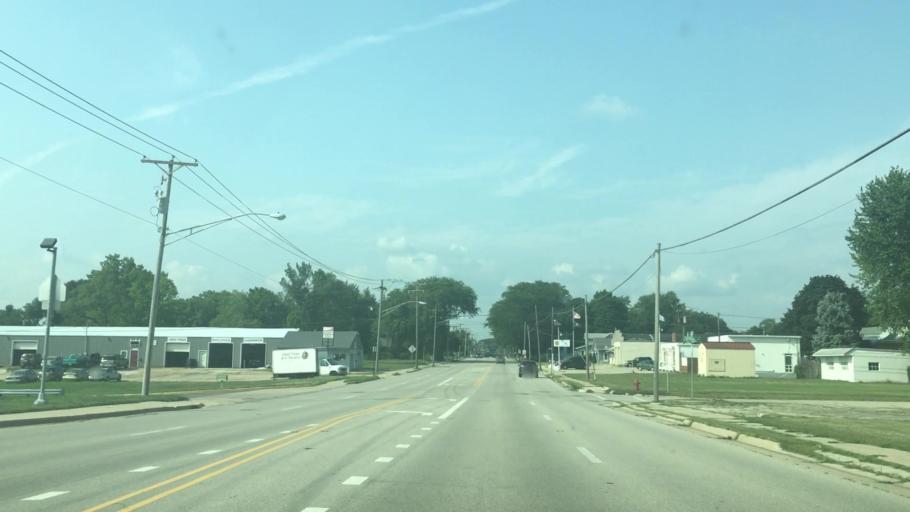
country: US
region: Illinois
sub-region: DeKalb County
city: DeKalb
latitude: 41.9138
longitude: -88.7534
